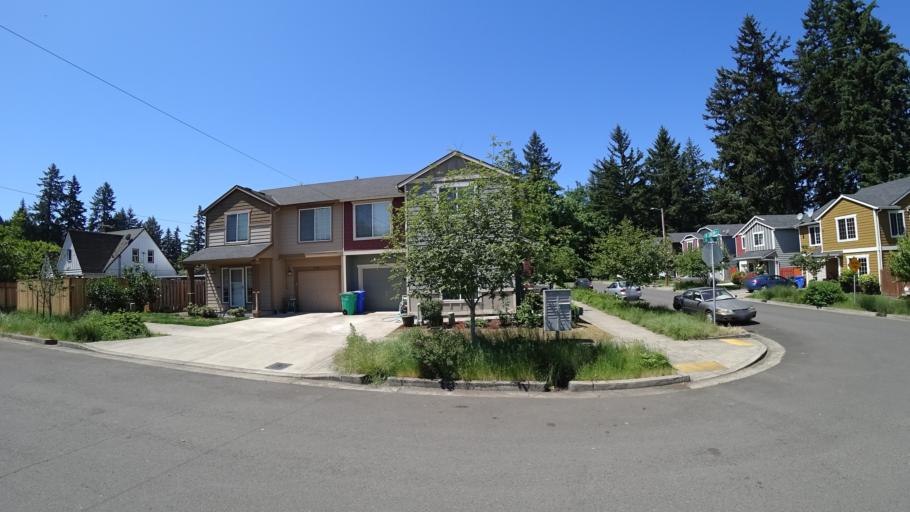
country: US
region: Oregon
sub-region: Clackamas County
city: Happy Valley
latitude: 45.4782
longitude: -122.5181
